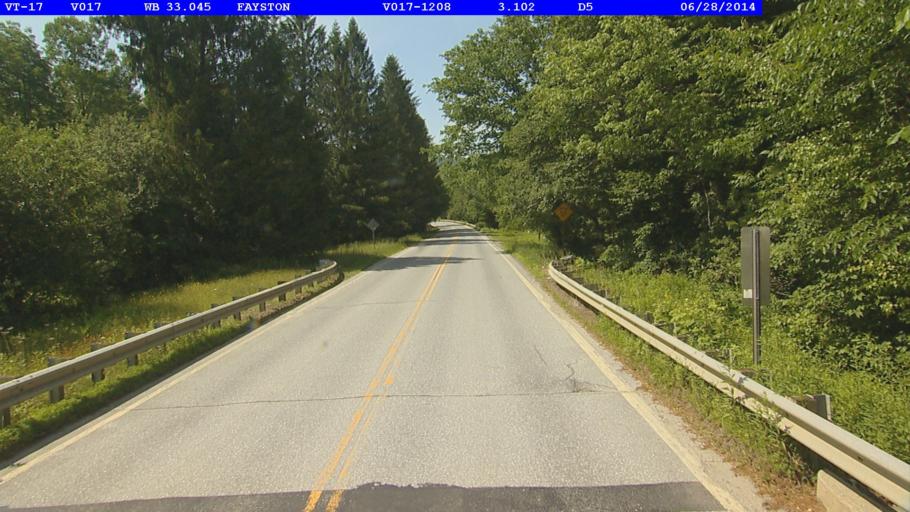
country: US
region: Vermont
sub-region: Washington County
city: Waterbury
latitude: 44.1942
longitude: -72.8899
